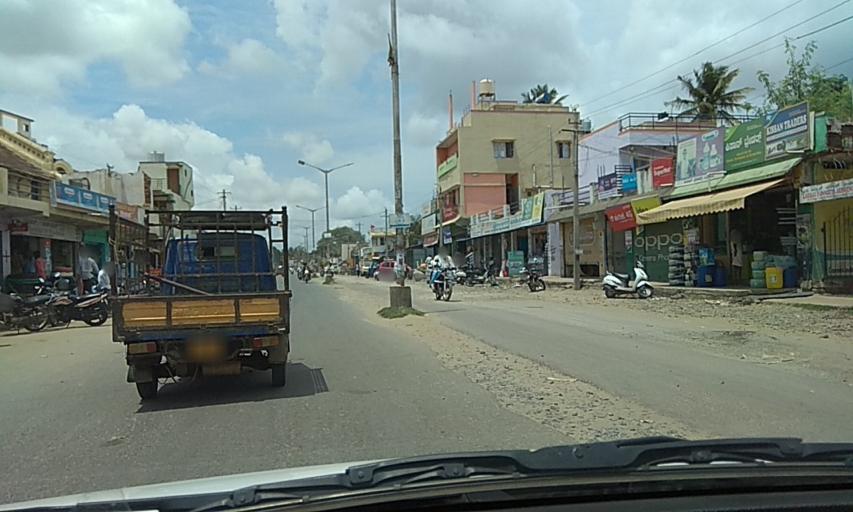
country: IN
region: Karnataka
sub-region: Chamrajnagar
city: Gundlupet
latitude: 11.8081
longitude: 76.6938
